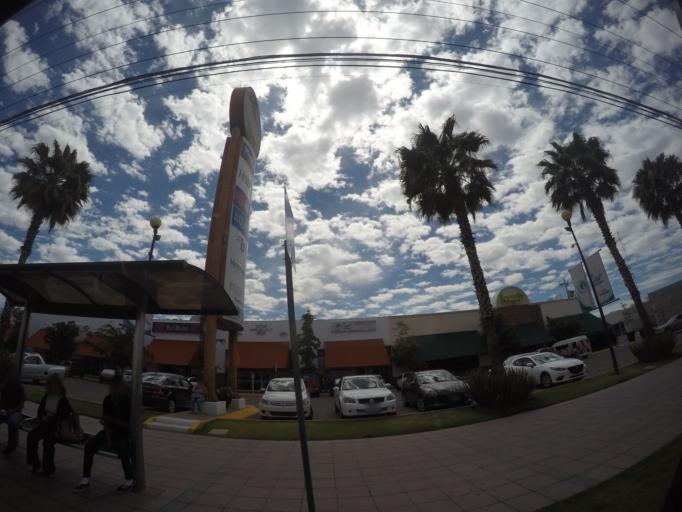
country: MX
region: Guanajuato
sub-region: Leon
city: San Jose de Duran (Los Troncoso)
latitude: 21.0952
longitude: -101.6637
